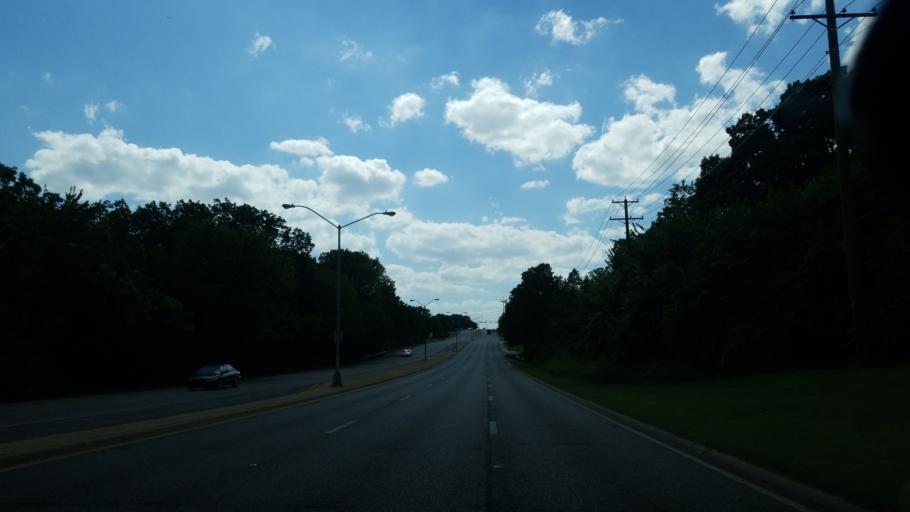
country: US
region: Texas
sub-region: Dallas County
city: Balch Springs
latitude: 32.7635
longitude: -96.6942
